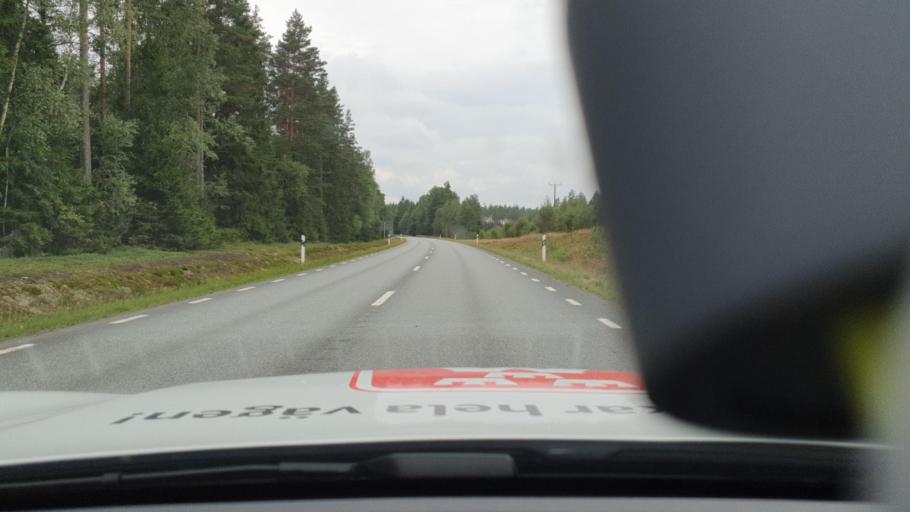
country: SE
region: Joenkoeping
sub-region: Gislaveds Kommun
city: Gislaved
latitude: 57.4216
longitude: 13.6050
